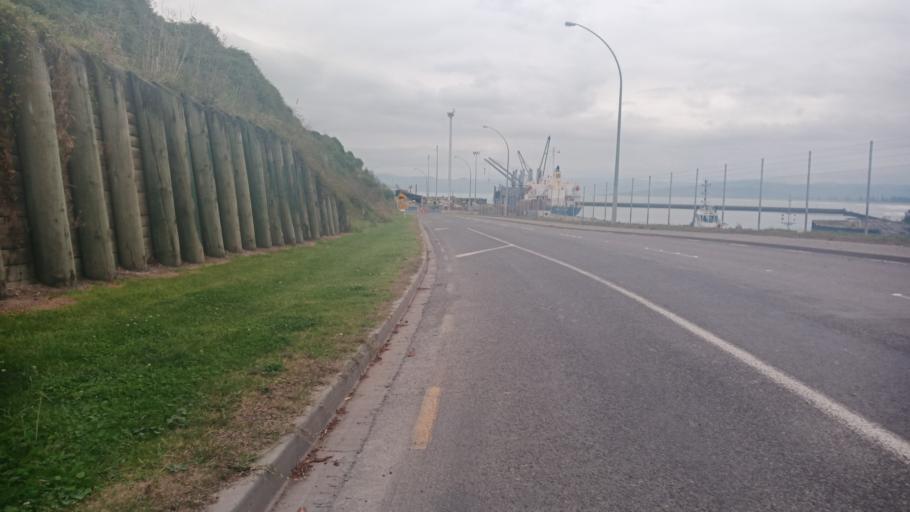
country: NZ
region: Gisborne
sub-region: Gisborne District
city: Gisborne
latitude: -38.6734
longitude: 178.0281
